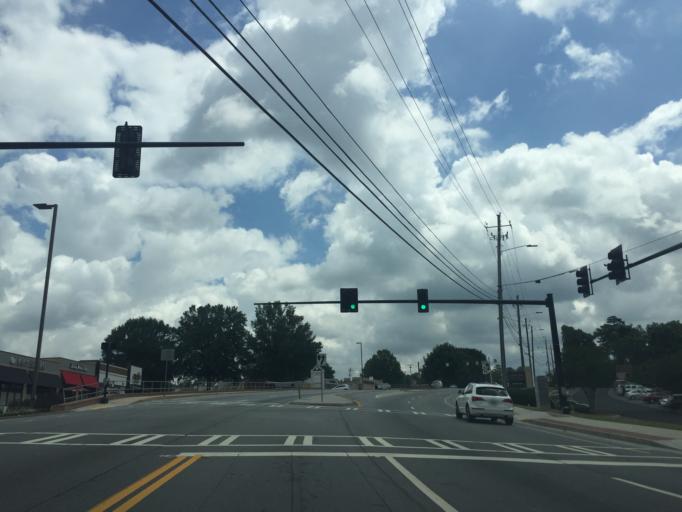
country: US
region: Georgia
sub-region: DeKalb County
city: North Druid Hills
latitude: 33.8261
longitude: -84.3329
